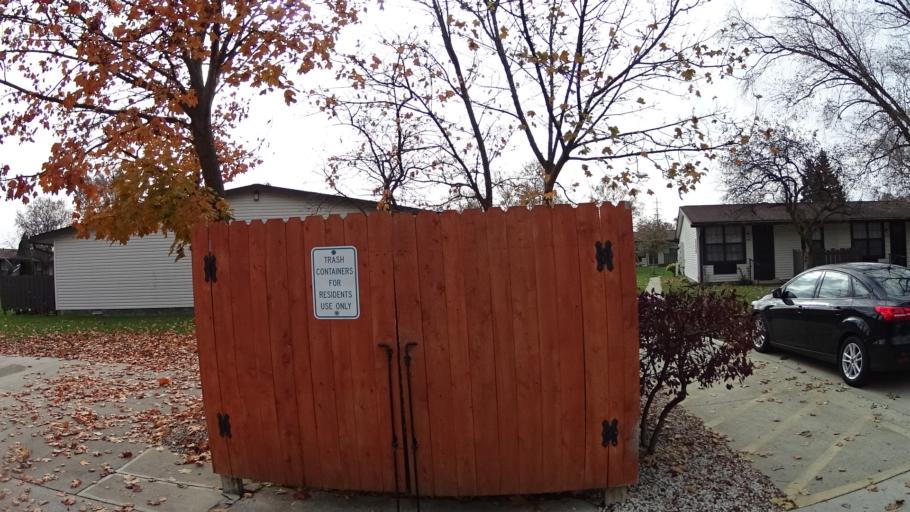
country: US
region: Ohio
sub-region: Lorain County
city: Elyria
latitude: 41.3596
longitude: -82.0773
